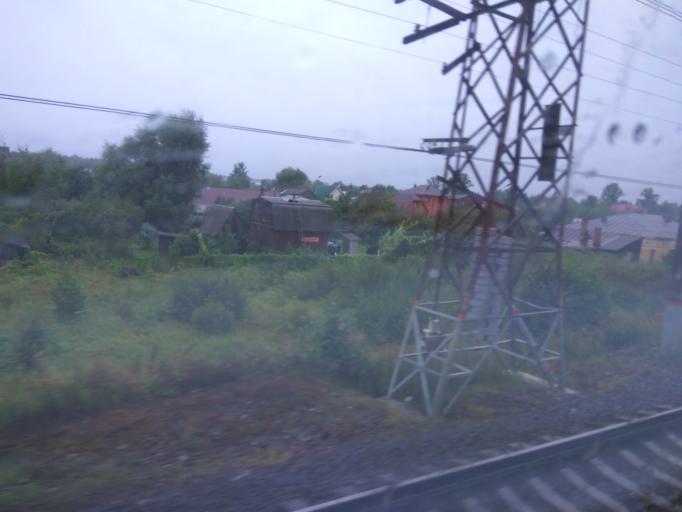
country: RU
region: Moskovskaya
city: Zhilevo
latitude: 54.9803
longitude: 38.0340
